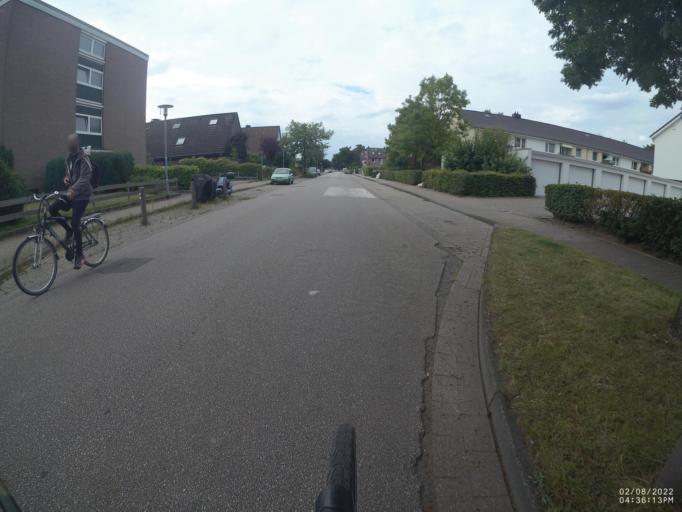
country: DE
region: Lower Saxony
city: Oldenburg
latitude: 53.1655
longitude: 8.1943
